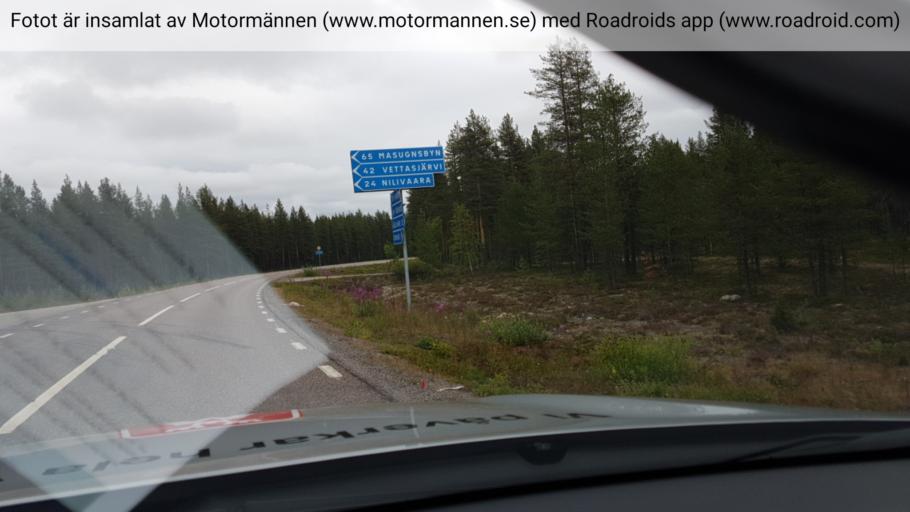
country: SE
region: Norrbotten
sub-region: Gallivare Kommun
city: Gaellivare
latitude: 67.0769
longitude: 21.3372
